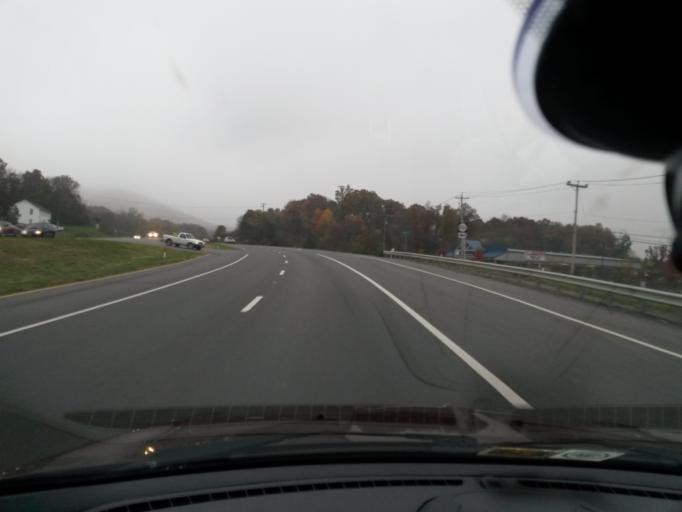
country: US
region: Virginia
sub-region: Botetourt County
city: Cloverdale
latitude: 37.3785
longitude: -79.8904
